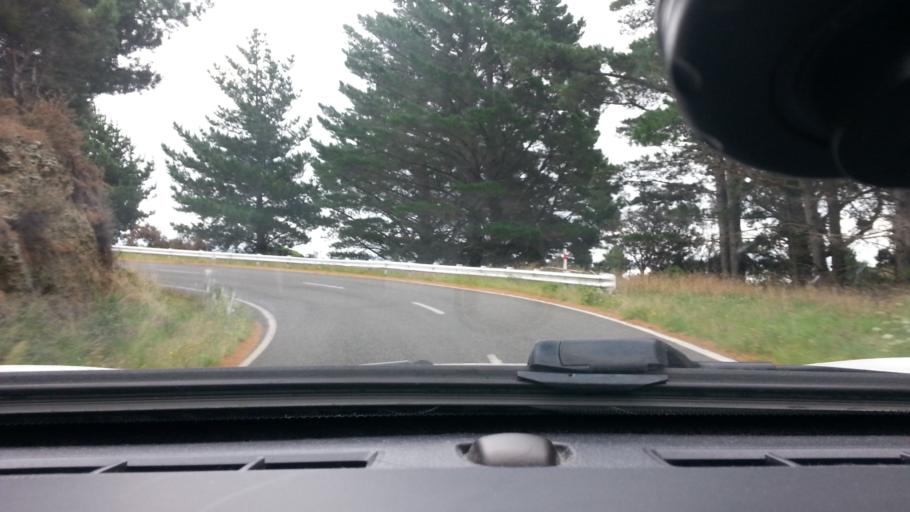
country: NZ
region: Wellington
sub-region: South Wairarapa District
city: Waipawa
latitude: -41.4325
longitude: 175.2256
